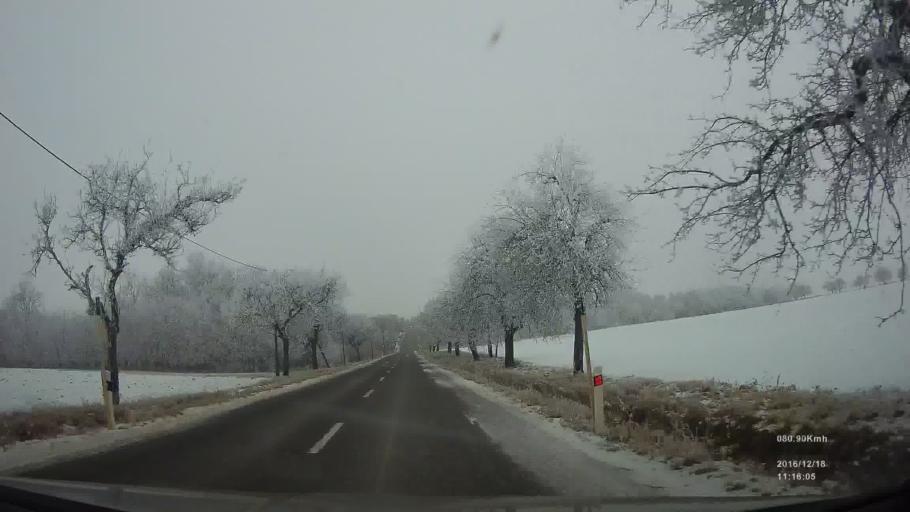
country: SK
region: Presovsky
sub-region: Okres Presov
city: Presov
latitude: 48.9133
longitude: 21.3248
